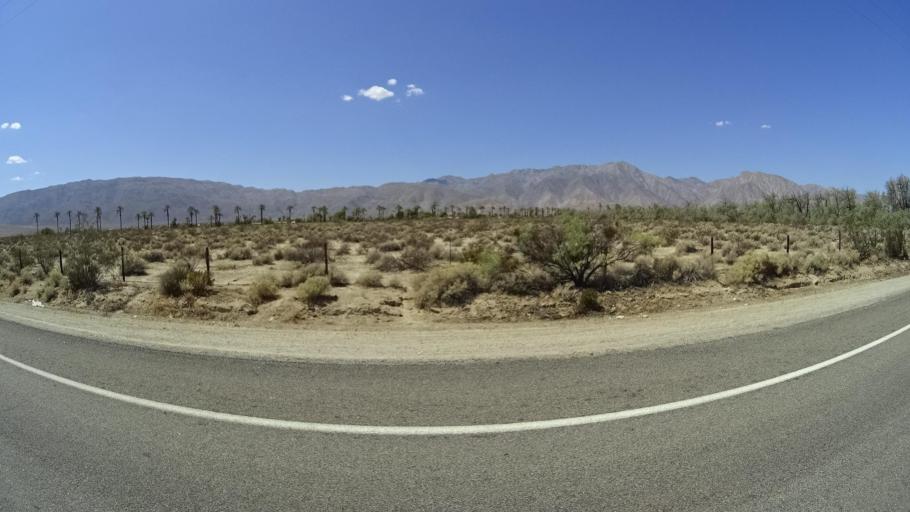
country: US
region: California
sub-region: San Diego County
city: Borrego Springs
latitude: 33.2341
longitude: -116.3479
